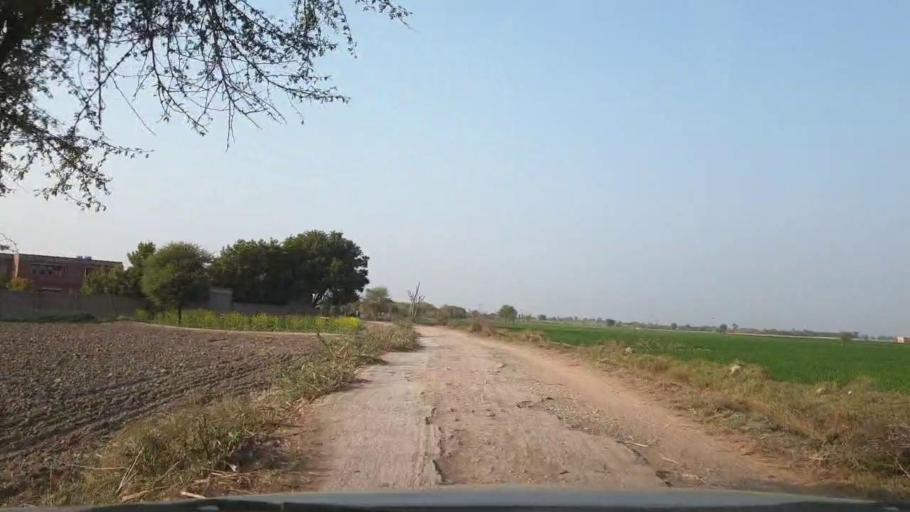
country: PK
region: Sindh
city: Tando Adam
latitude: 25.6804
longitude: 68.6341
